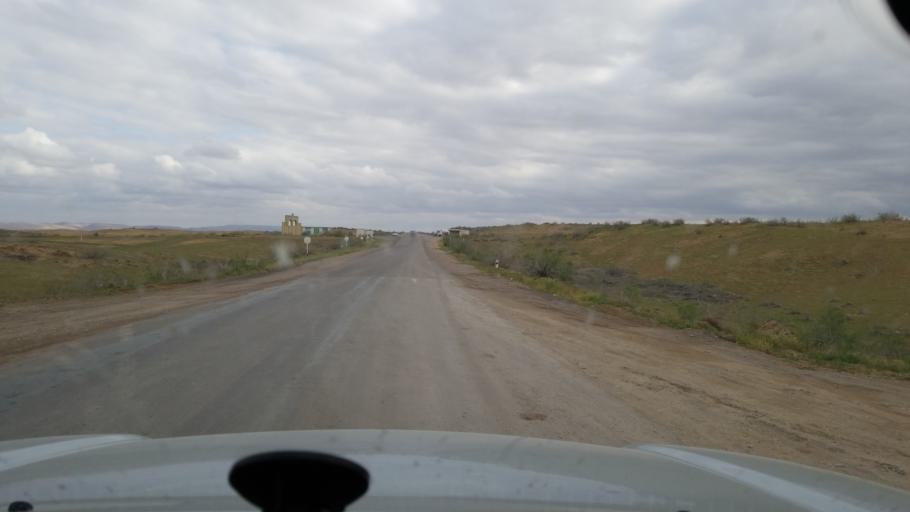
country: TM
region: Mary
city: Serhetabat
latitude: 35.9884
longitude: 62.6267
